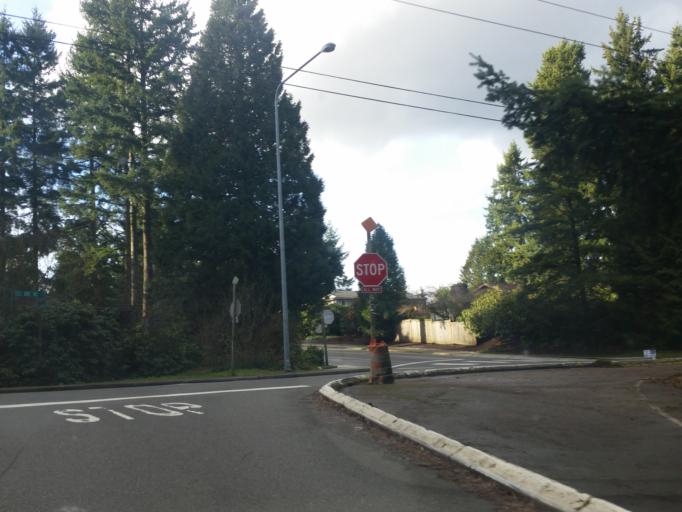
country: US
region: Washington
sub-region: King County
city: Kingsgate
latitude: 47.7301
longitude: -122.1637
